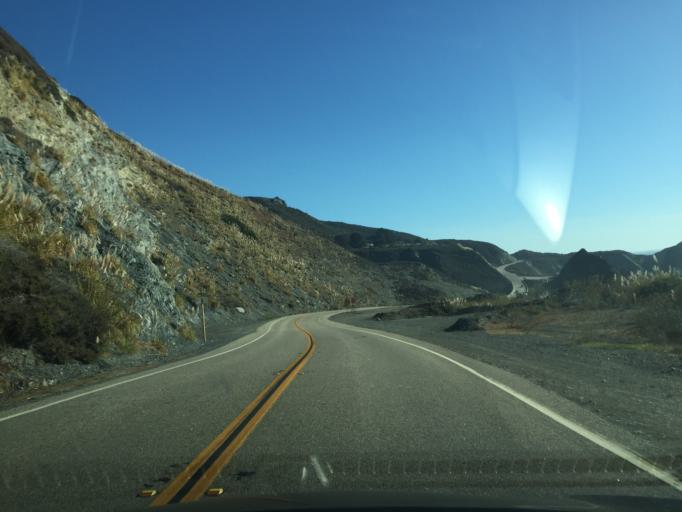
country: US
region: California
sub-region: Monterey County
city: King City
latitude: 35.8978
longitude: -121.4600
